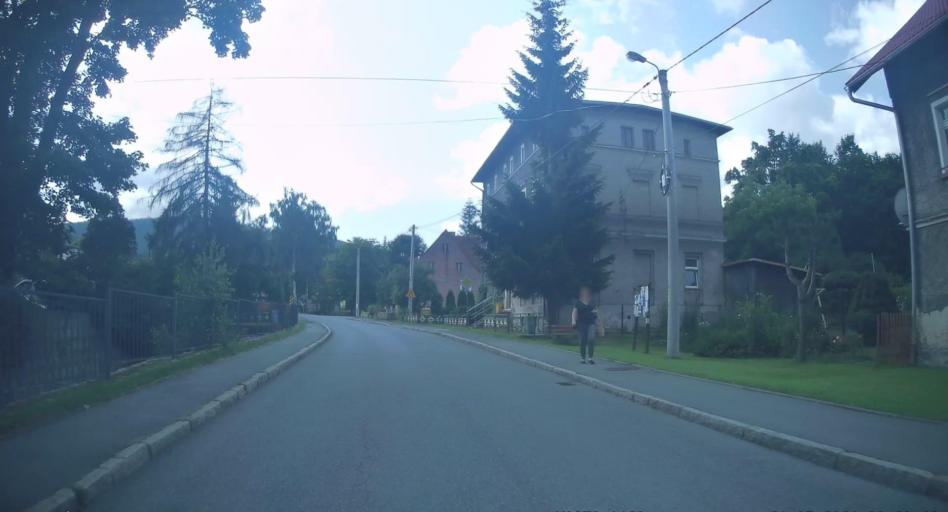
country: PL
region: Lower Silesian Voivodeship
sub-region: Powiat walbrzyski
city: Walim
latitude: 50.7013
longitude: 16.4389
